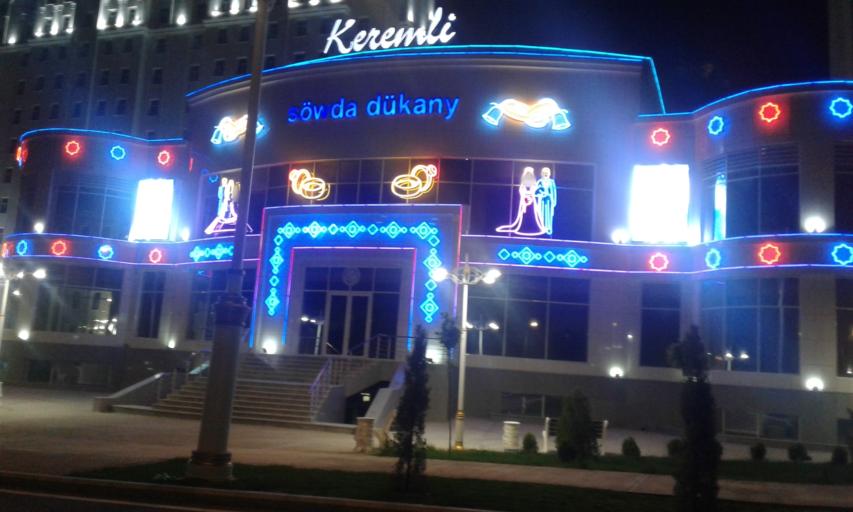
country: TM
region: Ahal
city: Ashgabat
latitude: 37.9400
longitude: 58.3571
